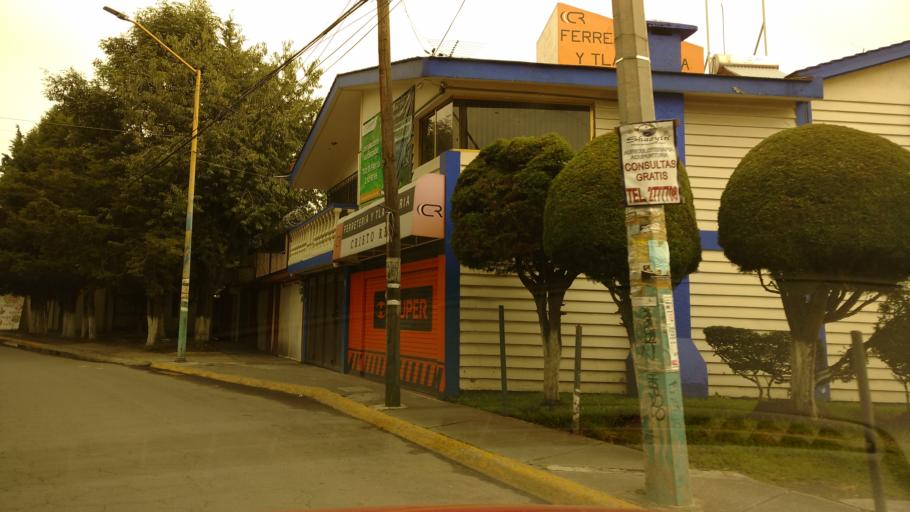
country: MX
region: Mexico
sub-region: Metepec
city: San Jorge Pueblo Nuevo
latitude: 19.2592
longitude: -99.6351
